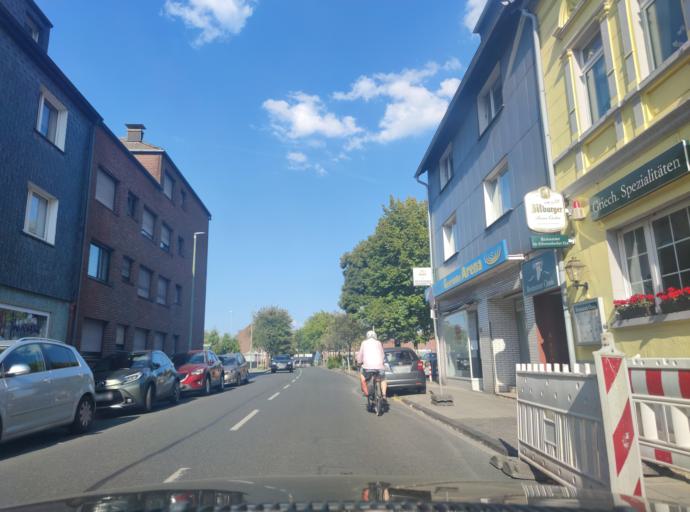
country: DE
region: North Rhine-Westphalia
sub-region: Regierungsbezirk Dusseldorf
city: Essen
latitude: 51.4850
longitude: 7.0615
